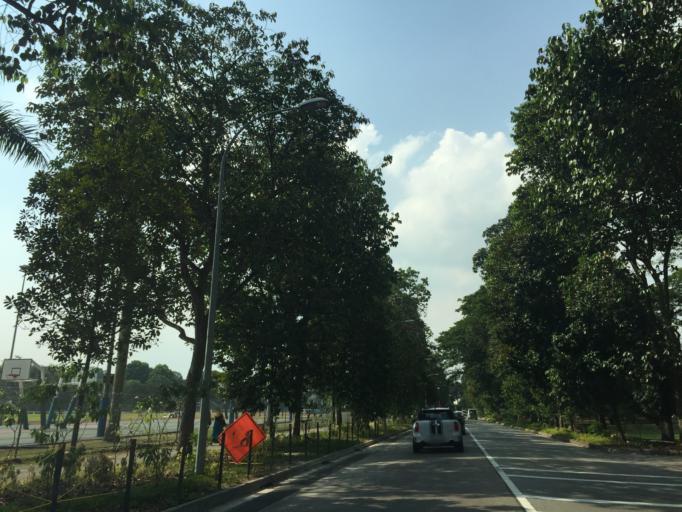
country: SG
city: Singapore
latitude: 1.3190
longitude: 103.8201
